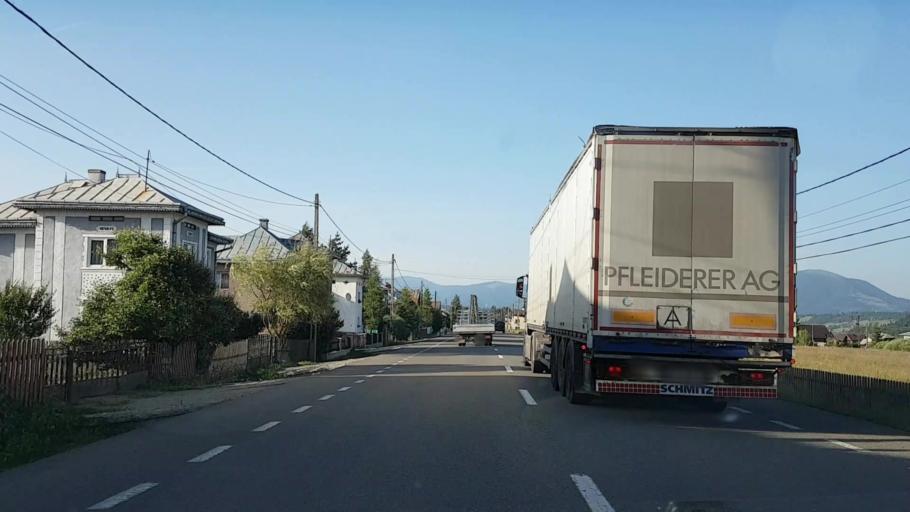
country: RO
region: Suceava
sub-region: Comuna Poiana Stampei
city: Poiana Stampei
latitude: 47.3140
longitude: 25.1311
